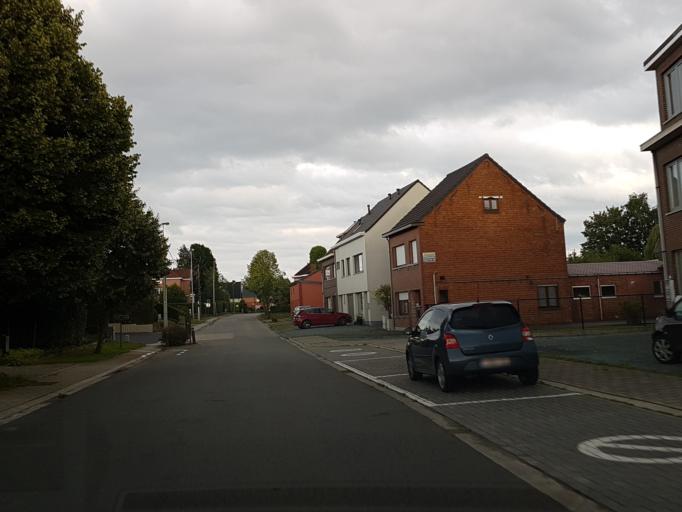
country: BE
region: Flanders
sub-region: Provincie Vlaams-Brabant
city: Opwijk
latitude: 50.9952
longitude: 4.1774
